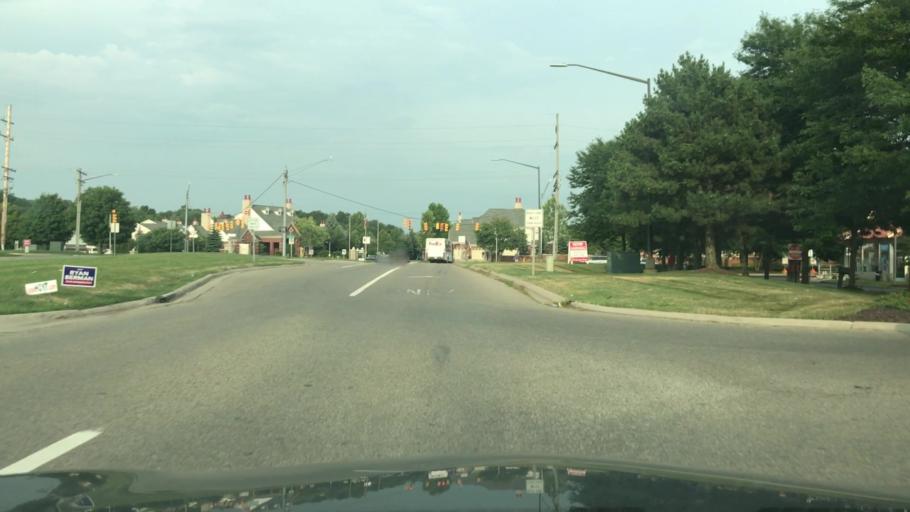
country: US
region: Michigan
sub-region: Oakland County
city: Wolverine Lake
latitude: 42.5349
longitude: -83.4393
